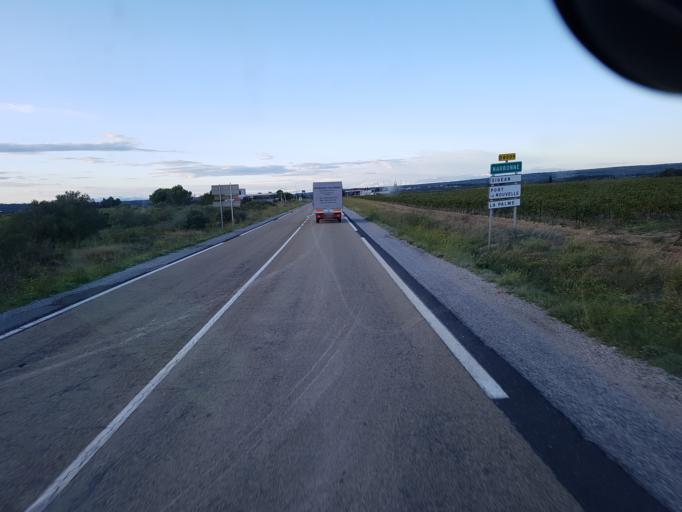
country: FR
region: Languedoc-Roussillon
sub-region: Departement de l'Aude
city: Leucate
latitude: 42.9409
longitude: 2.9899
